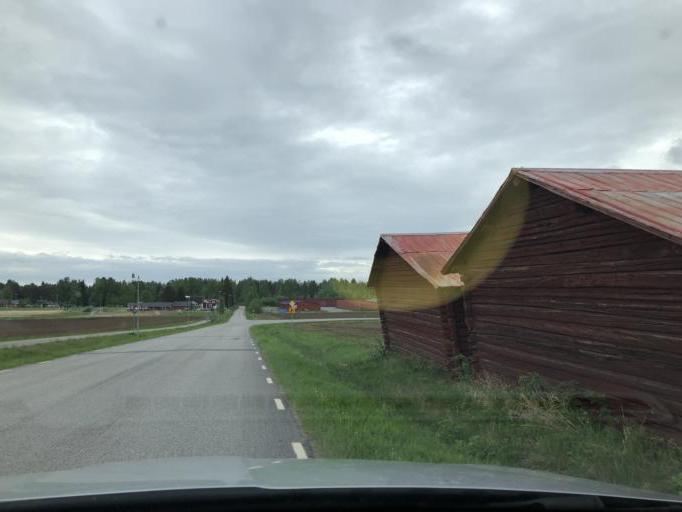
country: SE
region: Norrbotten
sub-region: Pitea Kommun
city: Bergsviken
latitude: 65.3816
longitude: 21.3132
